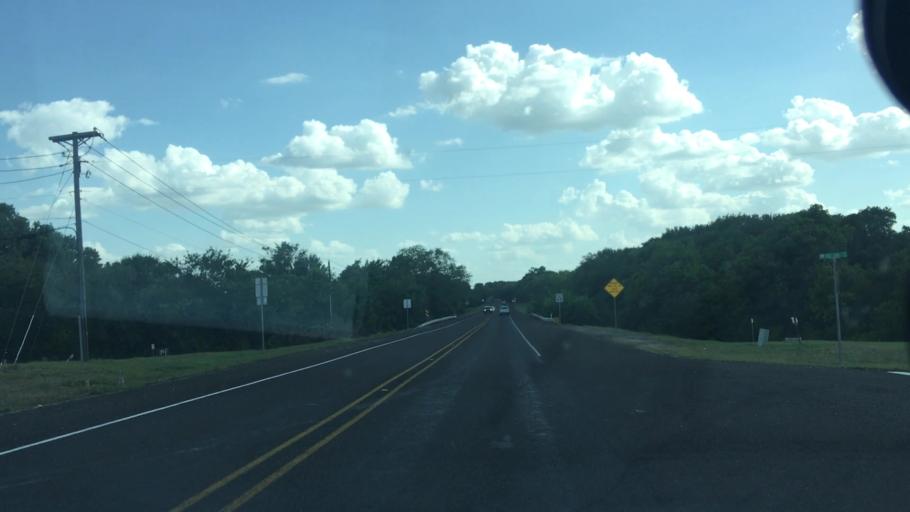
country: US
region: Texas
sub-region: Dallas County
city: Lancaster
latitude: 32.5789
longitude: -96.7561
